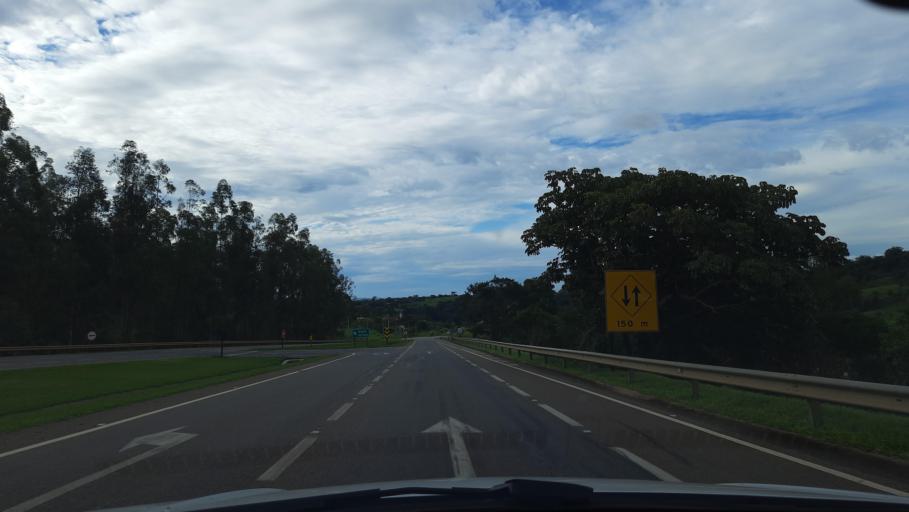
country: BR
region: Sao Paulo
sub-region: Sao Joao Da Boa Vista
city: Sao Joao da Boa Vista
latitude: -21.9632
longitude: -46.8337
